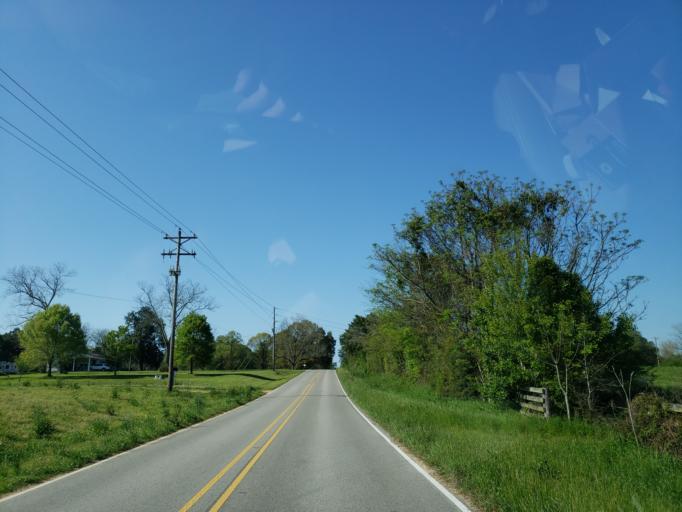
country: US
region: Mississippi
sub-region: Jones County
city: Ellisville
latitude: 31.5849
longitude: -89.3786
